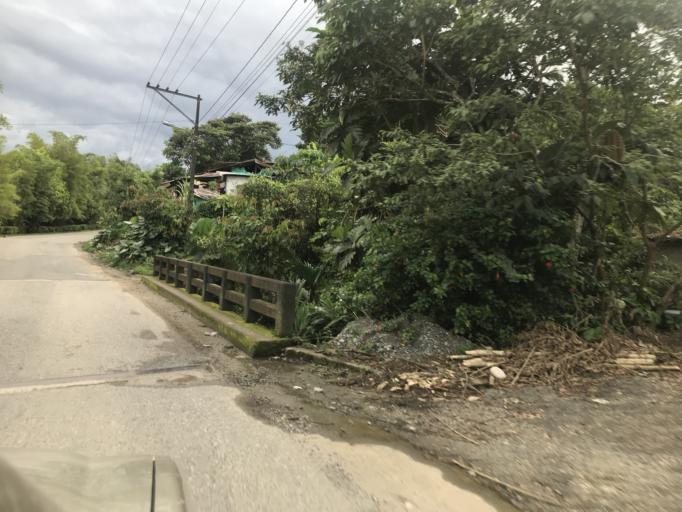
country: EC
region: Napo
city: Tena
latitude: -1.0394
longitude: -77.7875
